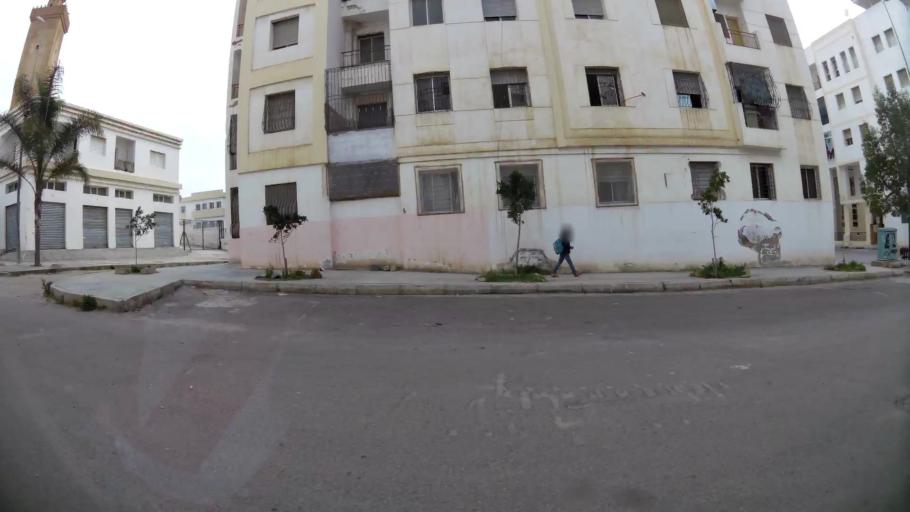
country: MA
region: Tanger-Tetouan
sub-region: Tanger-Assilah
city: Boukhalef
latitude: 35.7388
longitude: -5.8897
